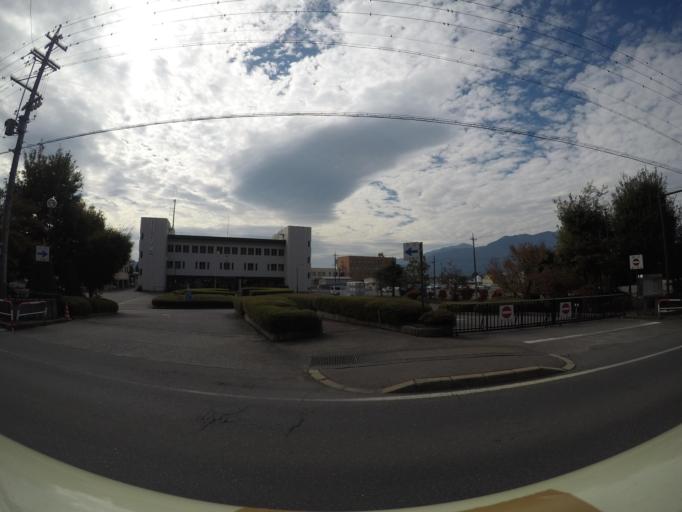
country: JP
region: Nagano
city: Ina
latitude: 35.8391
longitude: 137.9703
